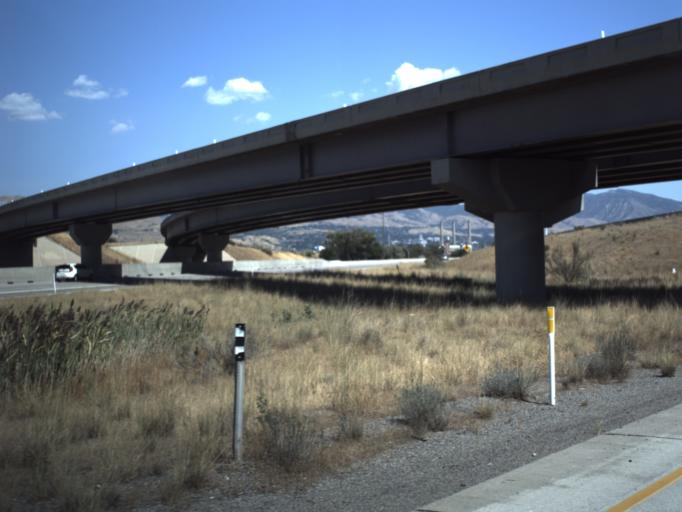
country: US
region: Utah
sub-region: Salt Lake County
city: Salt Lake City
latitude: 40.7652
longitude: -111.9487
